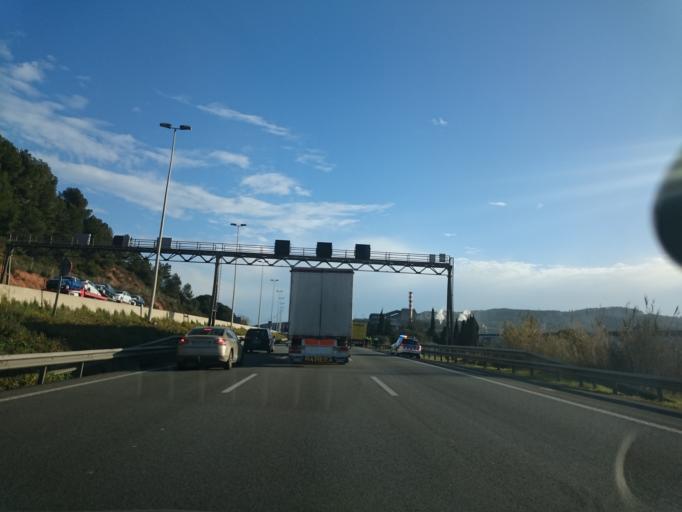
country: ES
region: Catalonia
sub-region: Provincia de Barcelona
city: Castellbisbal
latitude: 41.4601
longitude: 1.9807
